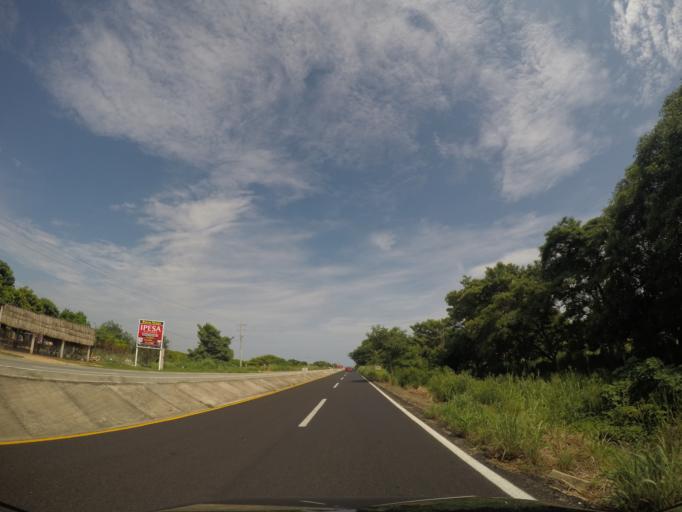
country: MX
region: Oaxaca
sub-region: Santa Maria Colotepec
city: Brisas de Zicatela
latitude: 15.8206
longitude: -97.0150
